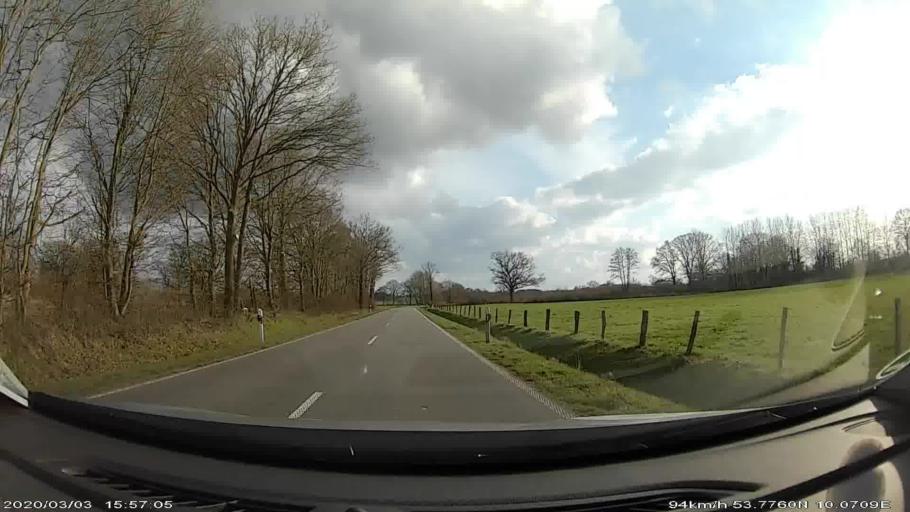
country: DE
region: Schleswig-Holstein
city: Tangstedt
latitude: 53.7774
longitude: 10.0703
